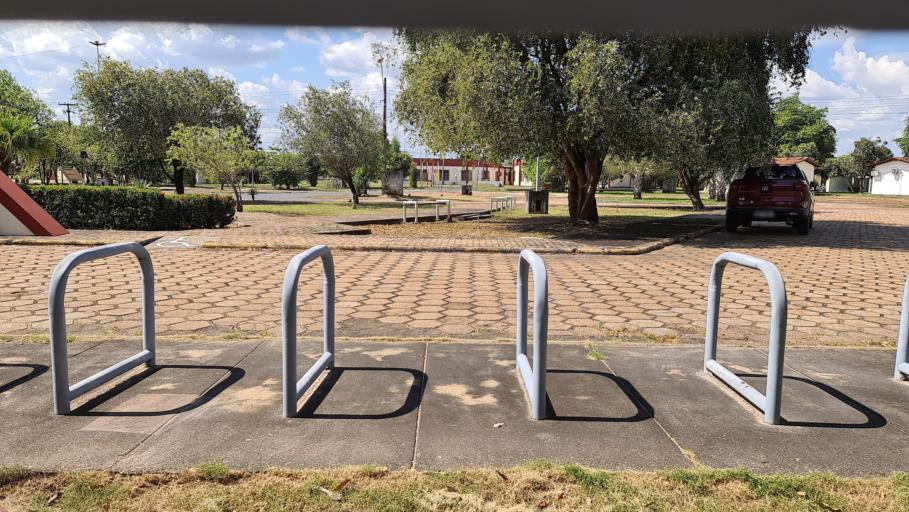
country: BR
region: Roraima
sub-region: Boa Vista
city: Boa Vista
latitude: 2.8314
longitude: -60.6957
